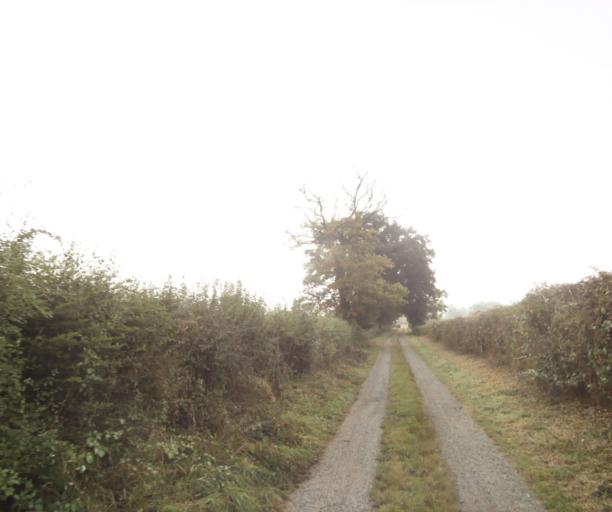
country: FR
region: Bourgogne
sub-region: Departement de Saone-et-Loire
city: Charolles
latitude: 46.4652
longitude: 4.3027
